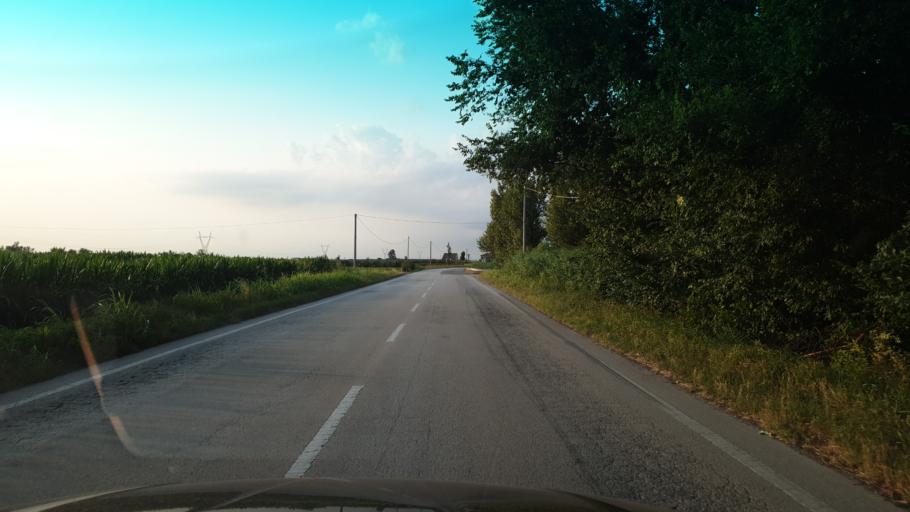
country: IT
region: Veneto
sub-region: Provincia di Rovigo
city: San Bellino
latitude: 45.0509
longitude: 11.5814
